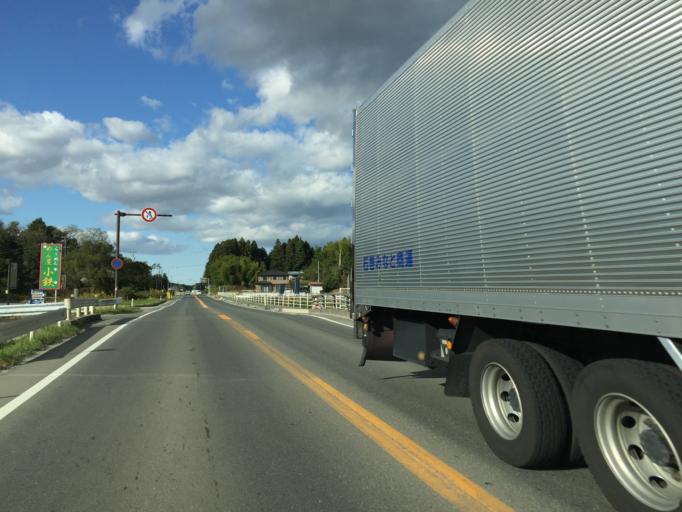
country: JP
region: Miyagi
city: Marumori
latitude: 37.8824
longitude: 140.9145
